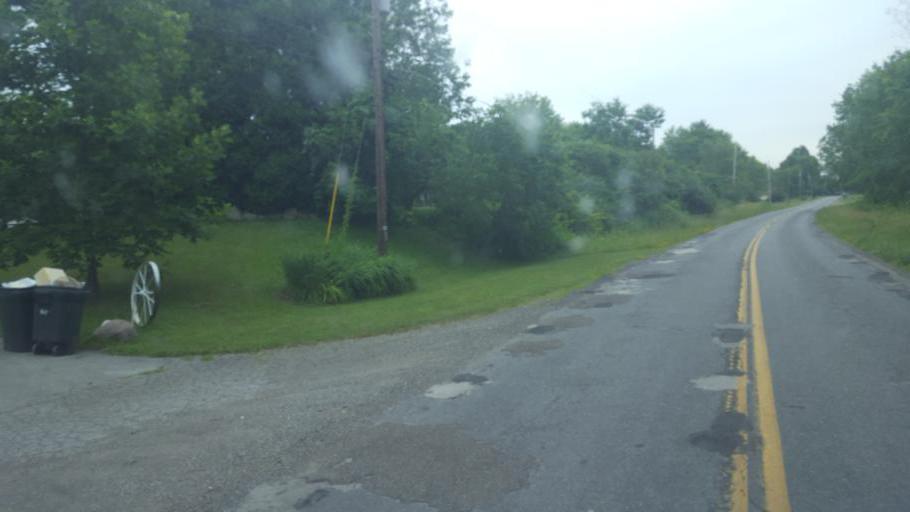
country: US
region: Ohio
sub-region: Trumbull County
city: South Canal
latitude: 41.1888
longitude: -81.0142
